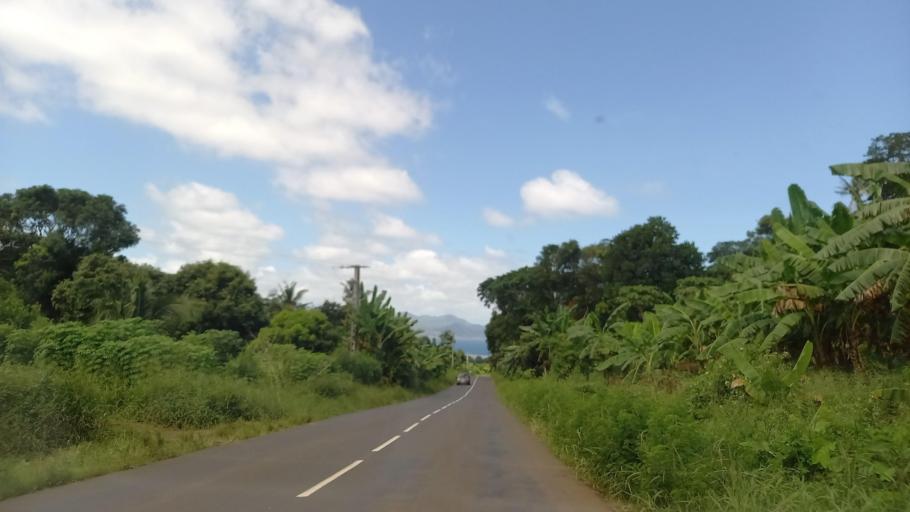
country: YT
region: Acoua
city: Acoua
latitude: -12.7388
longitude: 45.0533
